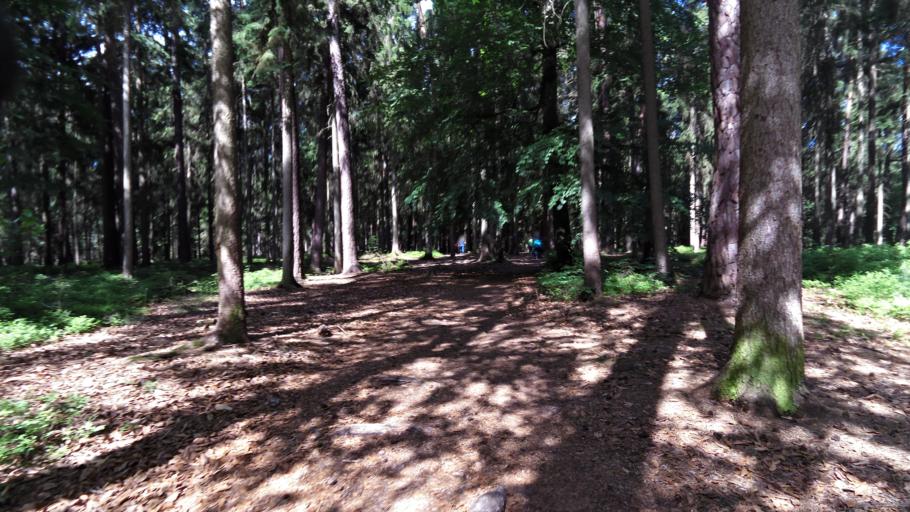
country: DE
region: Bavaria
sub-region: Regierungsbezirk Mittelfranken
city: Pleinfeld
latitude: 49.1132
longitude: 10.9632
